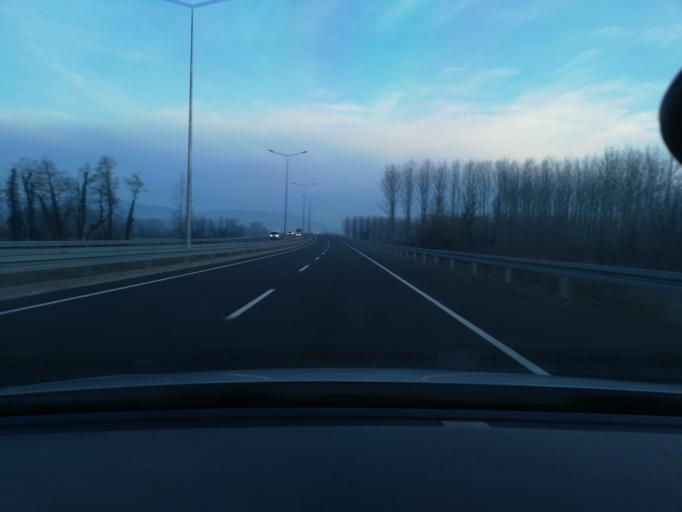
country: TR
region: Duzce
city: Duzce
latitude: 40.8133
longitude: 31.1692
